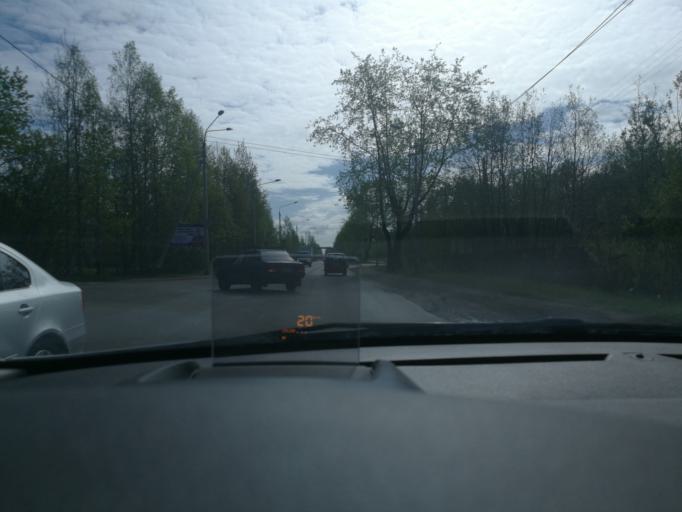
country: RU
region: Arkhangelskaya
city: Arkhangel'sk
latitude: 64.5954
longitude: 40.5731
